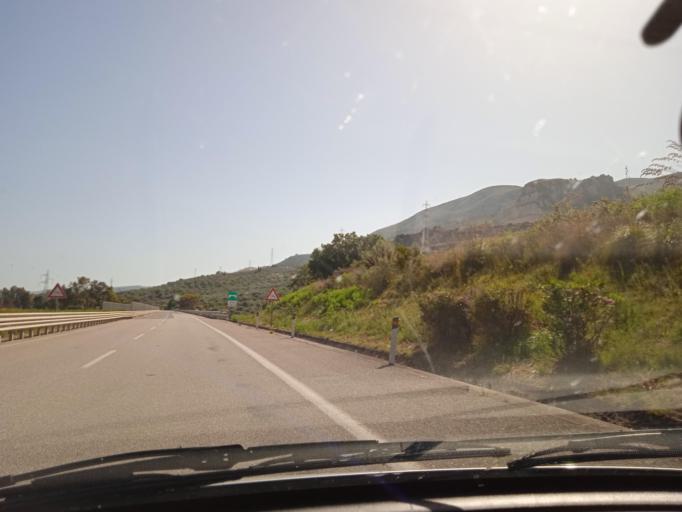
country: IT
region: Sicily
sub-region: Messina
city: Torrenova
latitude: 38.0843
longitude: 14.6876
